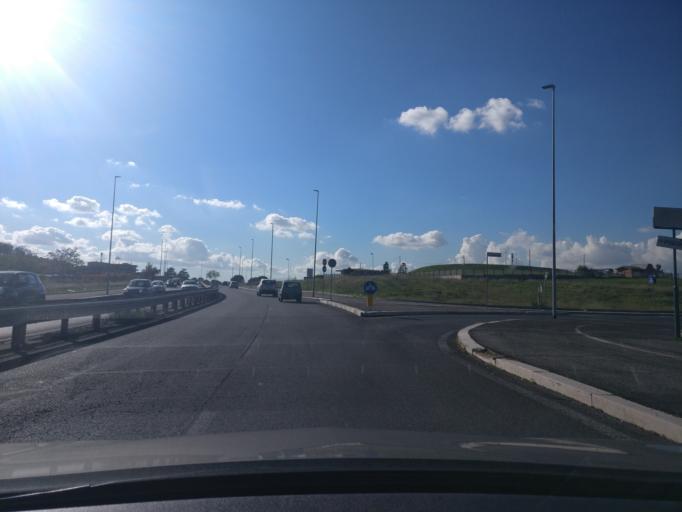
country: IT
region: Latium
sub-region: Citta metropolitana di Roma Capitale
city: Ciampino
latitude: 41.8555
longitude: 12.6136
